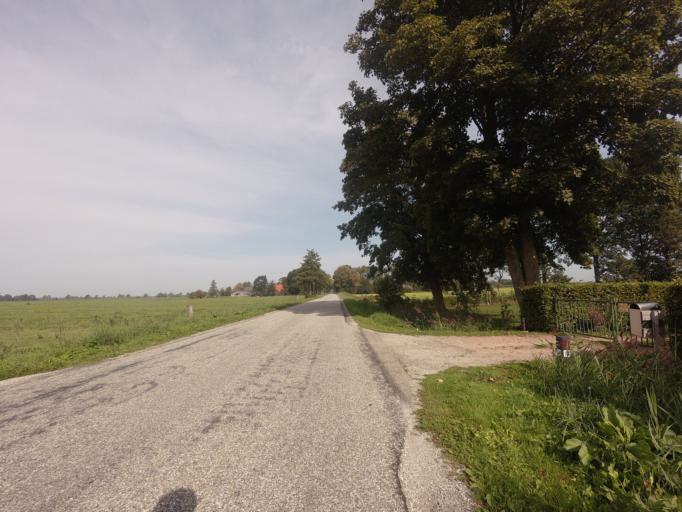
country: NL
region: Groningen
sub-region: Gemeente Leek
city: Leek
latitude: 53.1971
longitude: 6.3526
